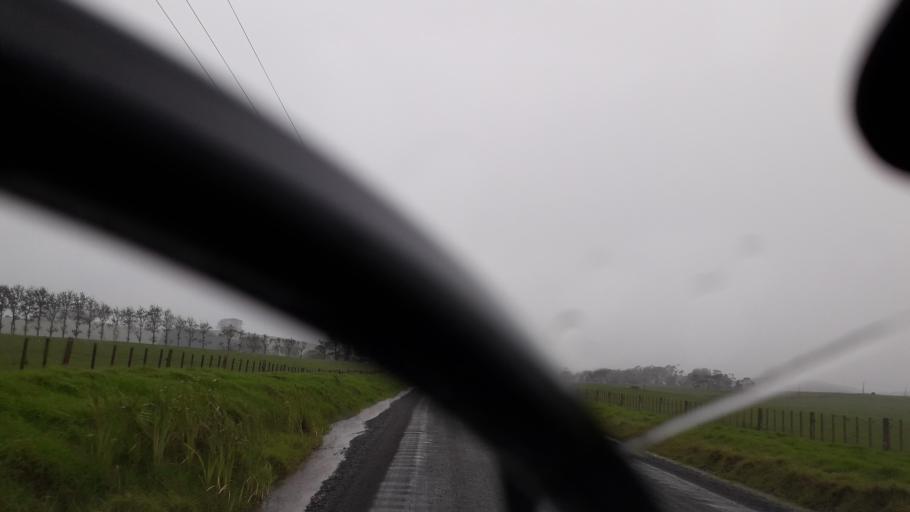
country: NZ
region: Northland
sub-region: Far North District
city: Kerikeri
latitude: -35.1381
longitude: 174.0330
